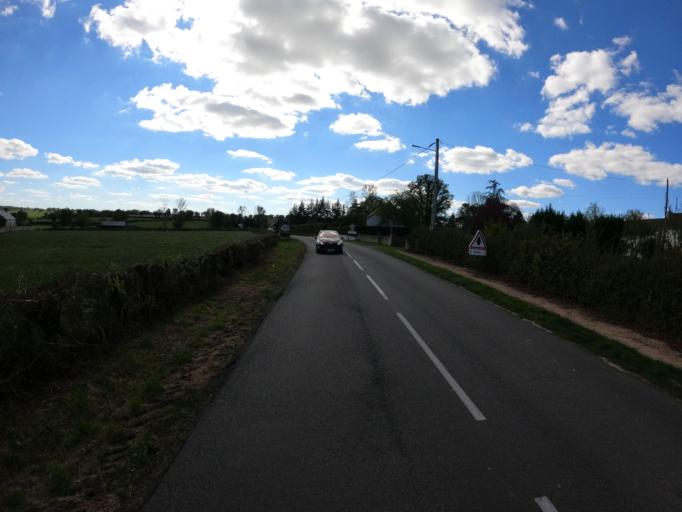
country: FR
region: Auvergne
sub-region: Departement de l'Allier
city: Doyet
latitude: 46.3809
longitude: 2.7786
